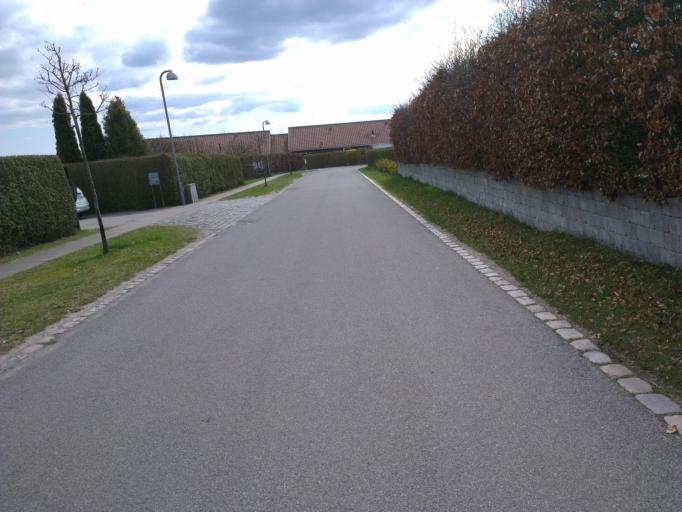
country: DK
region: Capital Region
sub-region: Frederikssund Kommune
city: Frederikssund
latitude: 55.8361
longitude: 12.0870
